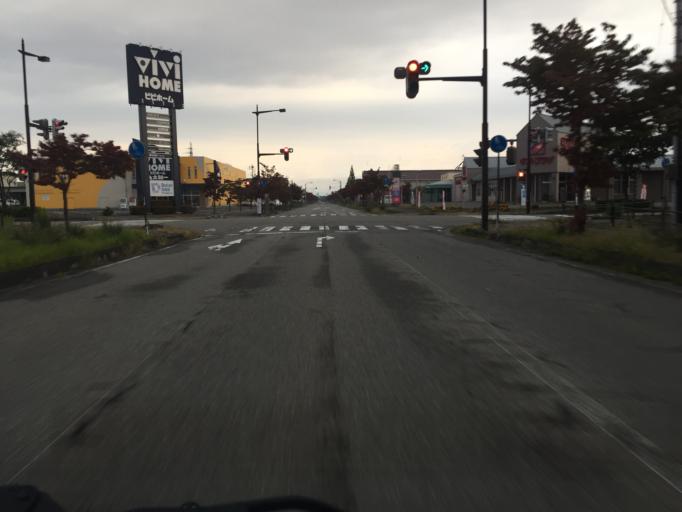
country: JP
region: Fukushima
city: Kitakata
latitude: 37.5189
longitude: 139.9148
